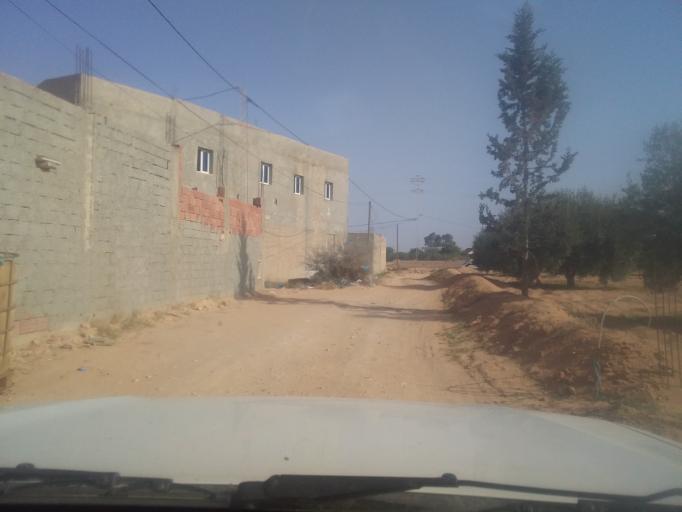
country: TN
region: Qabis
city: Matmata
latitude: 33.6085
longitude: 10.2797
